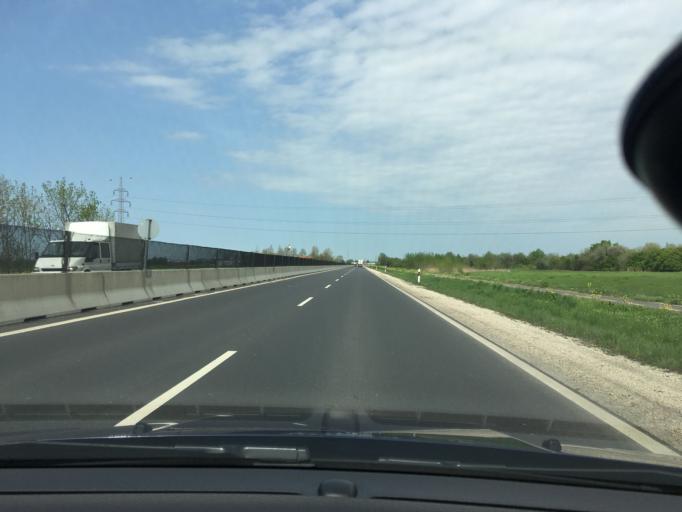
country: HU
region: Csongrad
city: Algyo
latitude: 46.3028
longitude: 20.1811
